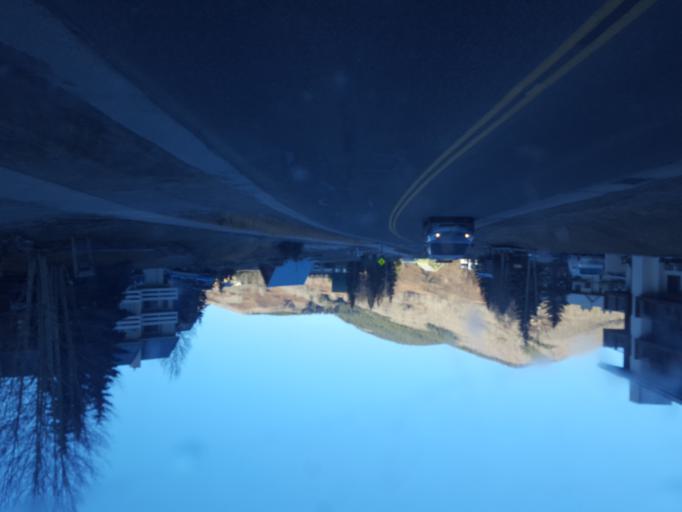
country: US
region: Colorado
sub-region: Gunnison County
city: Crested Butte
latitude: 38.9032
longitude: -106.9699
